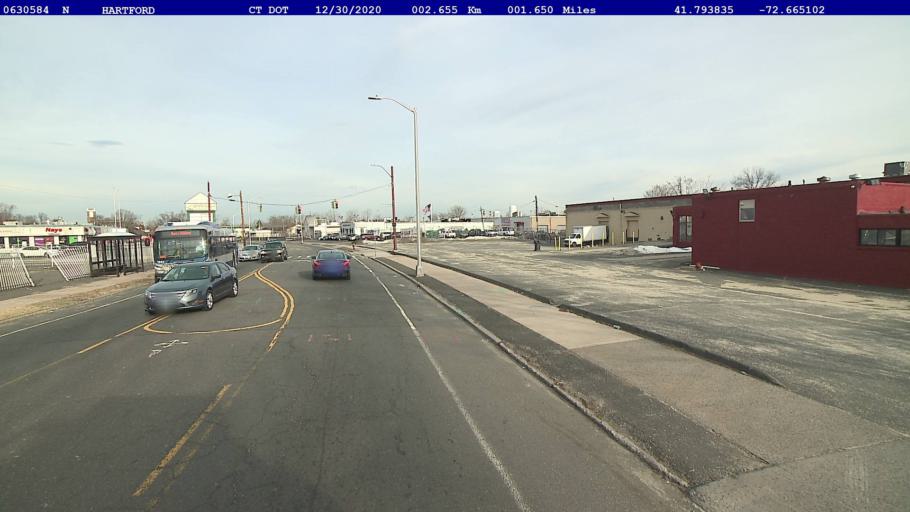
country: US
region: Connecticut
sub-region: Hartford County
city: Hartford
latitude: 41.7938
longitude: -72.6651
